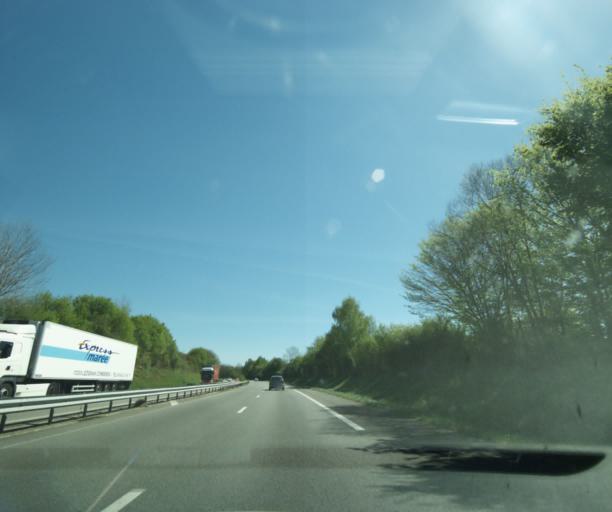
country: FR
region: Limousin
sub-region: Departement de la Haute-Vienne
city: Saint-Germain-les-Belles
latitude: 45.5958
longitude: 1.4510
